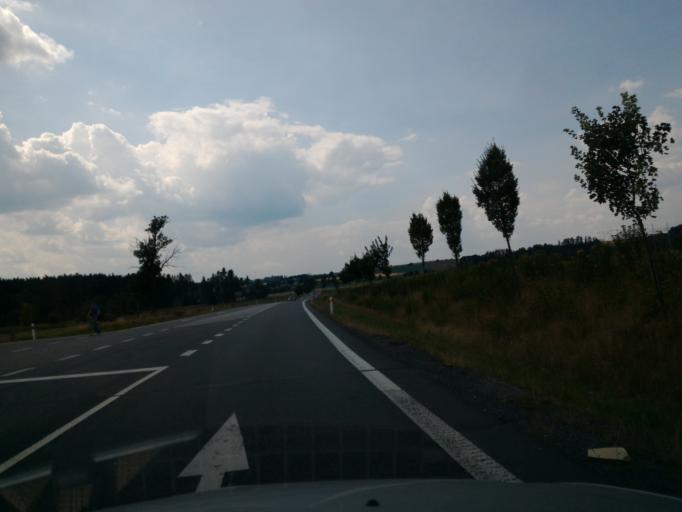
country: CZ
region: Vysocina
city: Bohdalov
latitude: 49.4779
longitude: 15.8555
